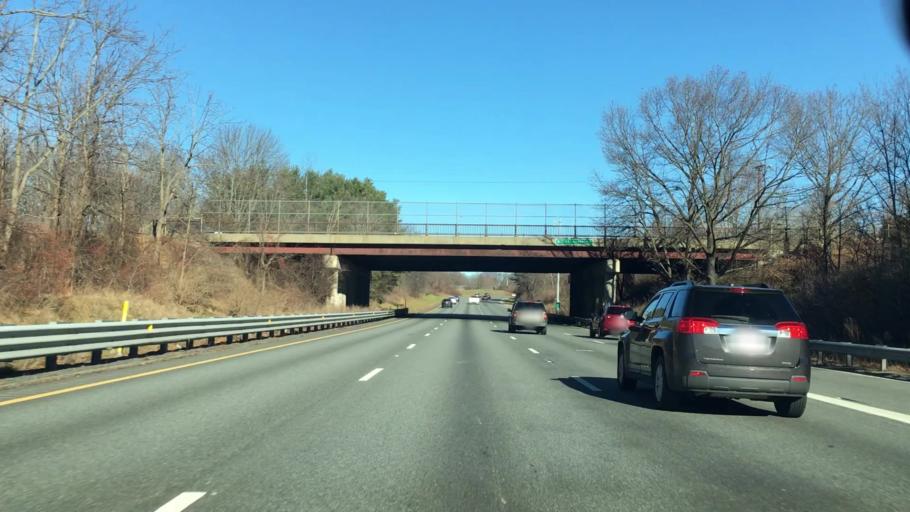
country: US
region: Massachusetts
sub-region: Essex County
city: Haverhill
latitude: 42.7824
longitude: -71.1149
